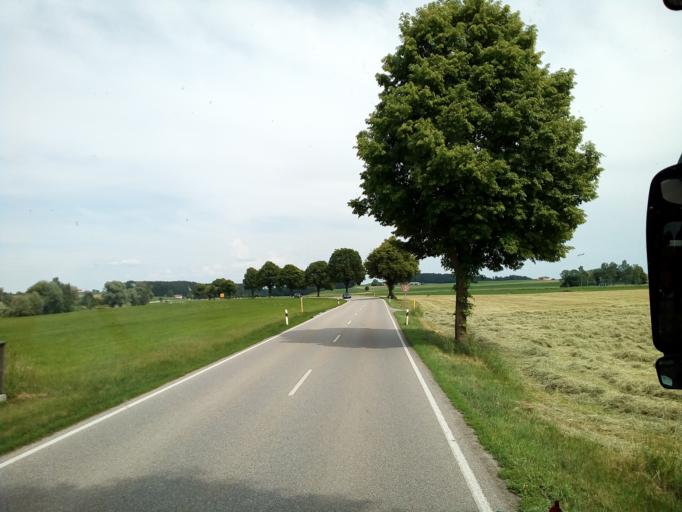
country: DE
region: Bavaria
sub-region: Upper Bavaria
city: Obing
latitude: 48.0002
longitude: 12.4141
